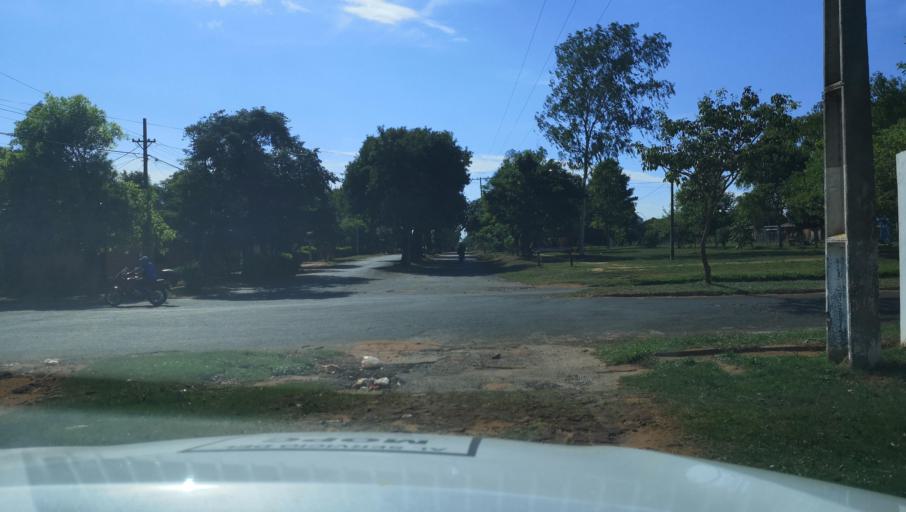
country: PY
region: Misiones
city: Santa Maria
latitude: -26.8929
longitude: -57.0315
